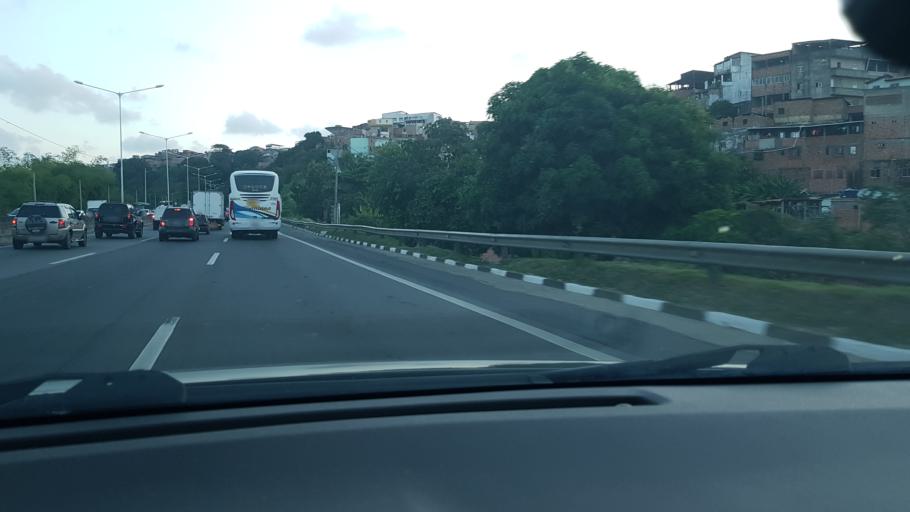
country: BR
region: Bahia
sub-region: Salvador
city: Salvador
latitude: -12.9325
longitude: -38.4715
